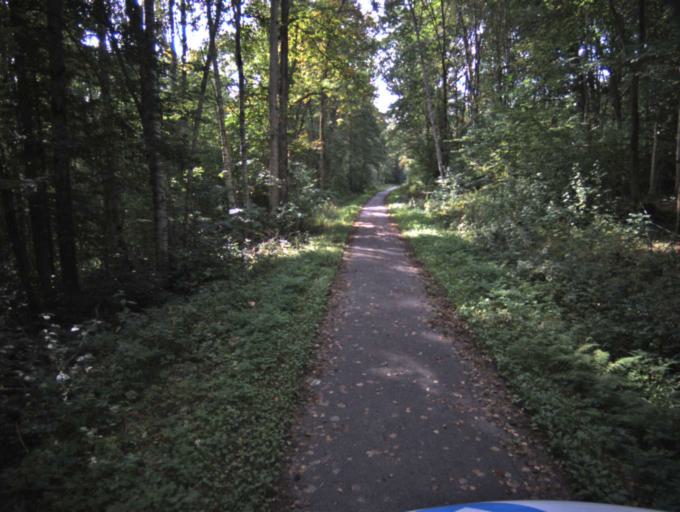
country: SE
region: Vaestra Goetaland
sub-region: Tranemo Kommun
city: Limmared
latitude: 57.6429
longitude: 13.3587
